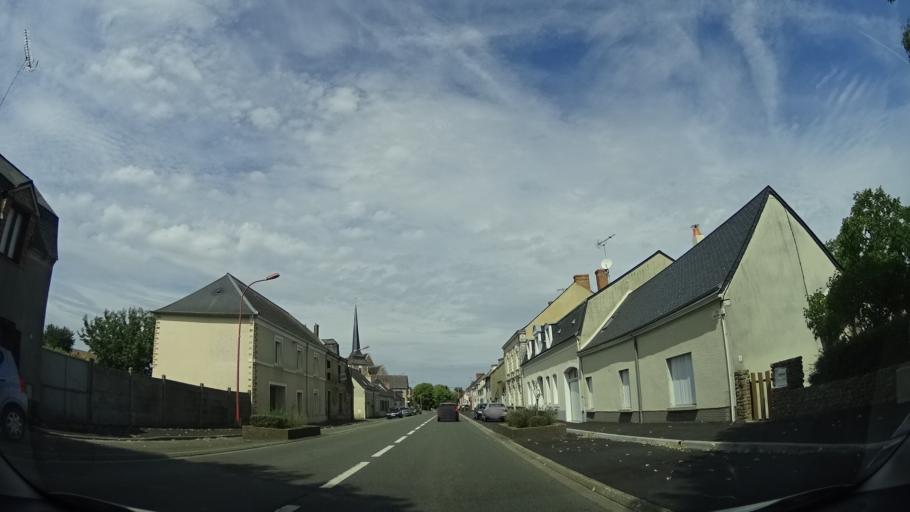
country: FR
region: Pays de la Loire
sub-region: Departement de la Sarthe
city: Bazouges-sur-le-Loir
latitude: 47.7461
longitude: -0.1486
